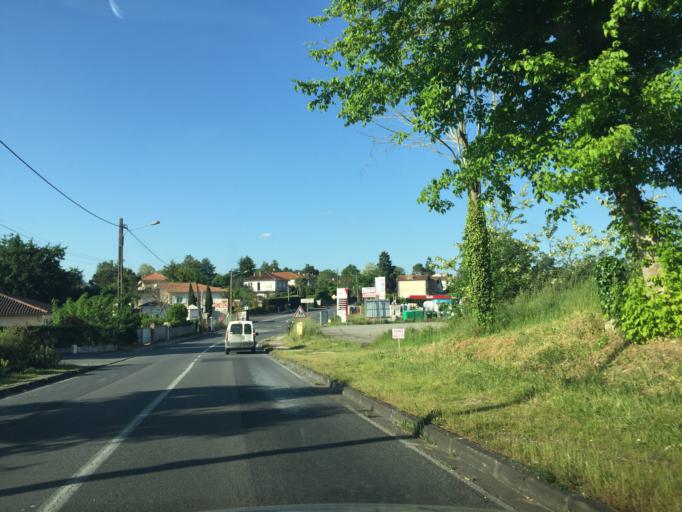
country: FR
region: Aquitaine
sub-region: Departement de la Dordogne
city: La Roche-Chalais
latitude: 45.1456
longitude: 0.0041
